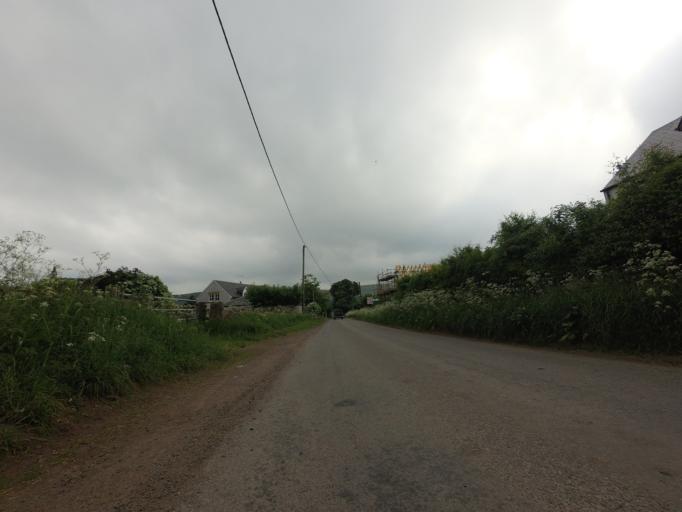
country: GB
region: Scotland
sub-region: Perth and Kinross
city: Kinross
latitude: 56.1699
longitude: -3.4461
